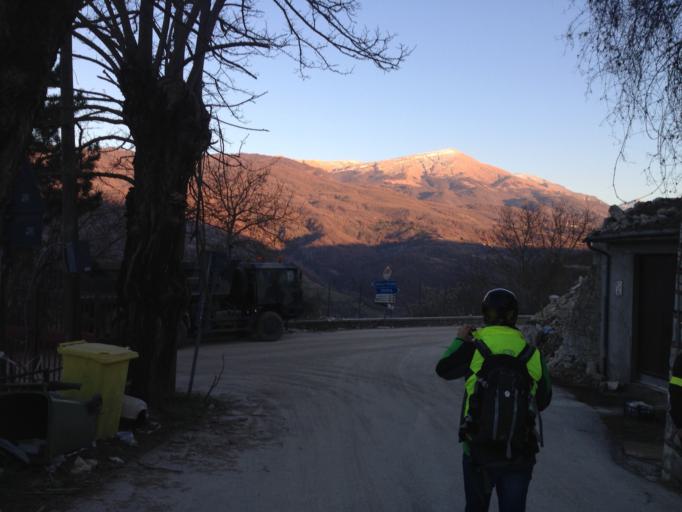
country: IT
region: Latium
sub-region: Provincia di Rieti
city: Accumoli
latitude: 42.6953
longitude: 13.2487
